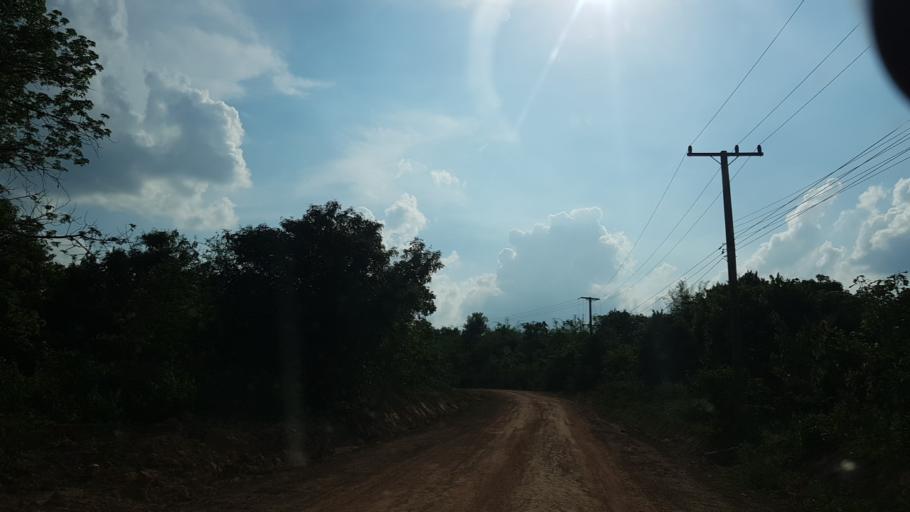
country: LA
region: Vientiane
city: Muang Phon-Hong
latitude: 18.3505
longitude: 102.2692
